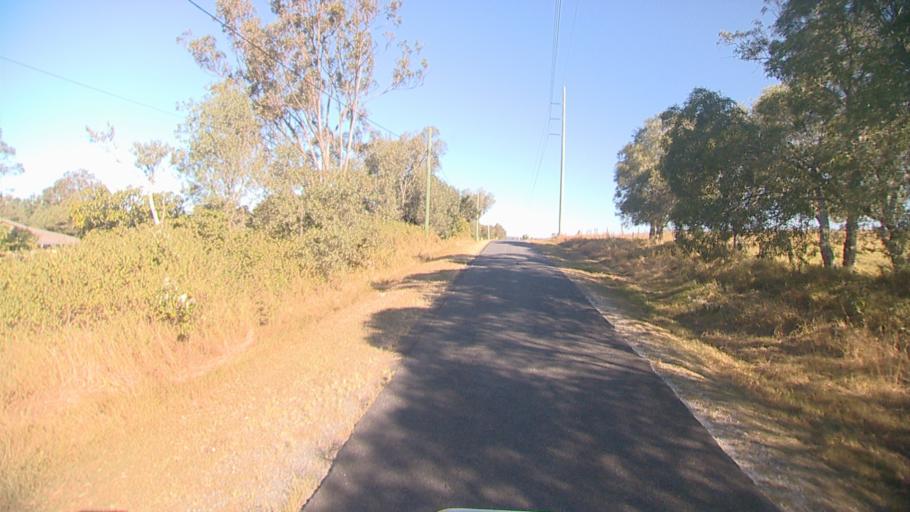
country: AU
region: Queensland
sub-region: Logan
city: Chambers Flat
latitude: -27.7695
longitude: 153.0601
